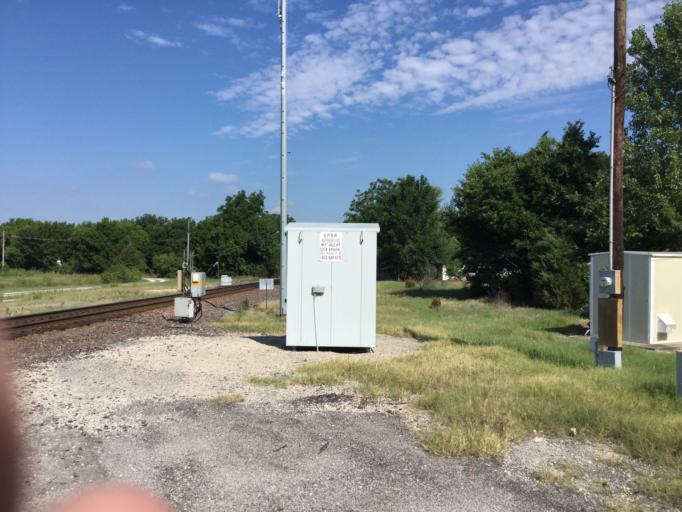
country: US
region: Kansas
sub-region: Montgomery County
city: Coffeyville
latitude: 37.0545
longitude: -95.7105
